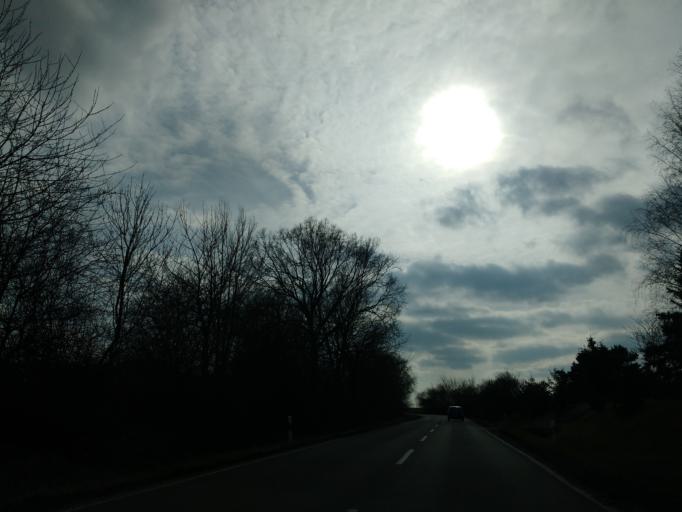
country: DE
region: Saxony-Anhalt
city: Schraplau
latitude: 51.4304
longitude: 11.6507
